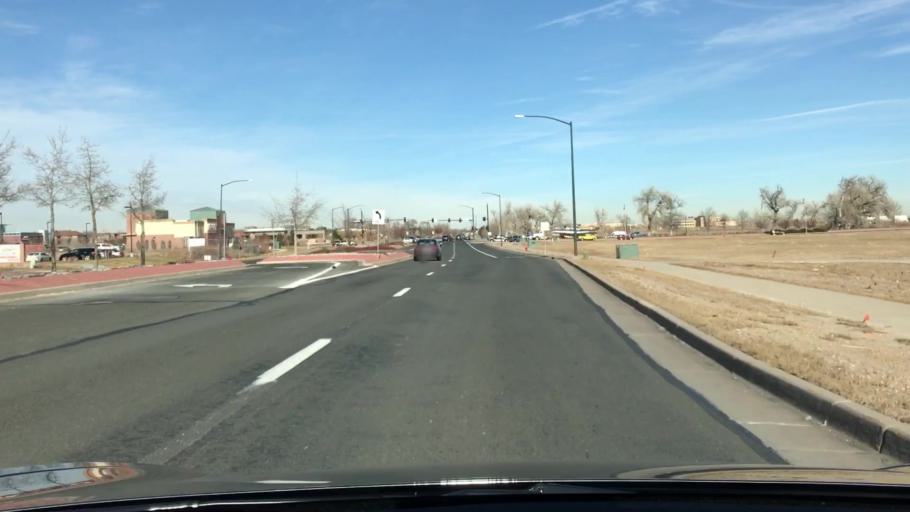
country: US
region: Colorado
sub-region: Adams County
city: Northglenn
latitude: 39.9410
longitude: -104.9967
